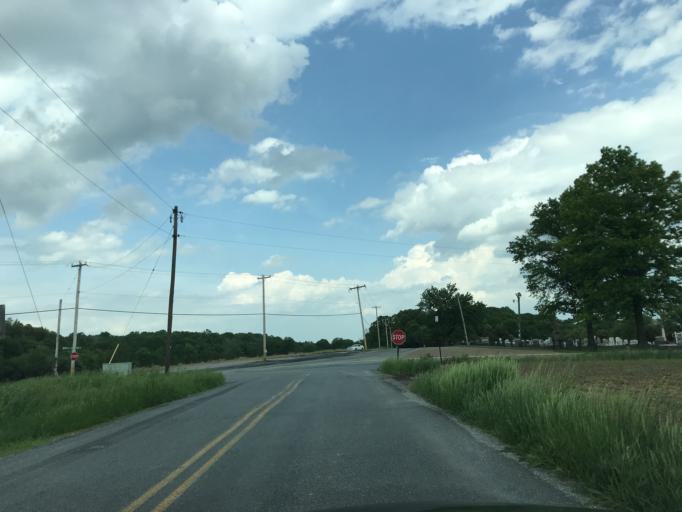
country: US
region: Pennsylvania
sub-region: York County
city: Susquehanna Trails
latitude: 39.7294
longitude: -76.3050
